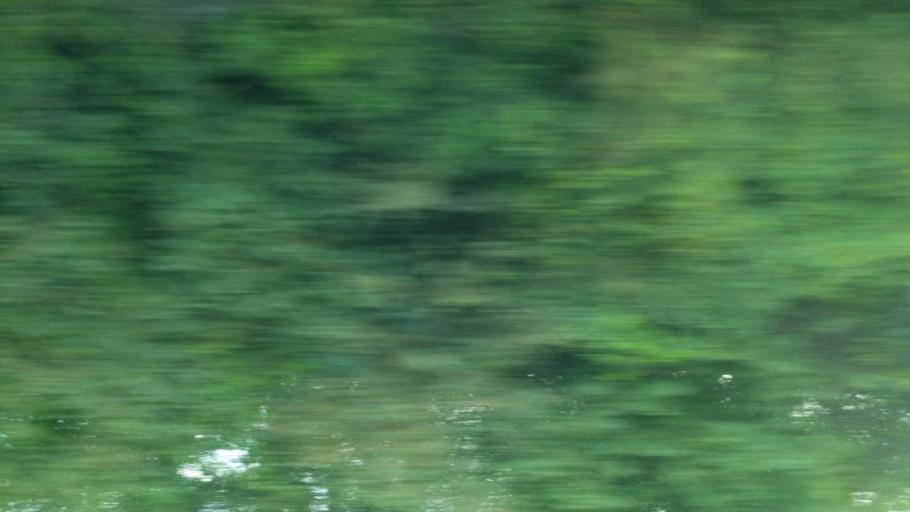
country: CZ
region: Central Bohemia
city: Uvaly
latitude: 50.0723
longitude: 14.7385
